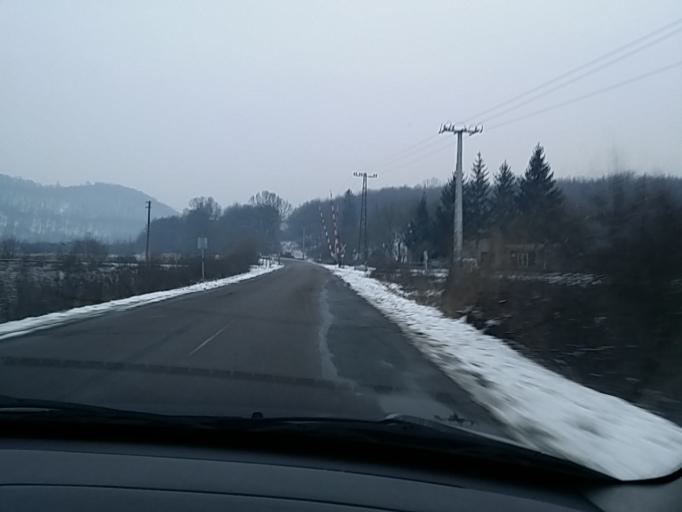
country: HU
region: Heves
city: Sirok
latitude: 47.9162
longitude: 20.1773
